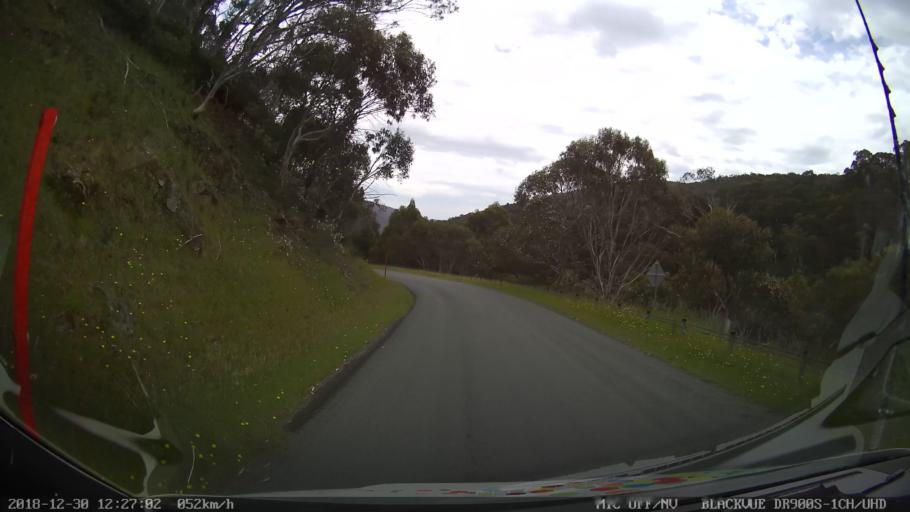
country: AU
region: New South Wales
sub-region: Snowy River
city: Jindabyne
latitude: -36.3340
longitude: 148.4901
